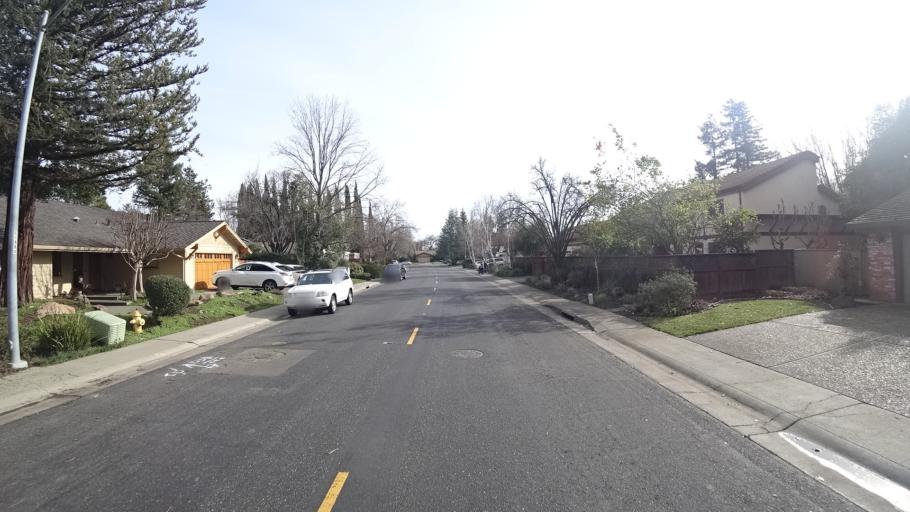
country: US
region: California
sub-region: Yolo County
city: Davis
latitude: 38.5395
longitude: -121.7007
